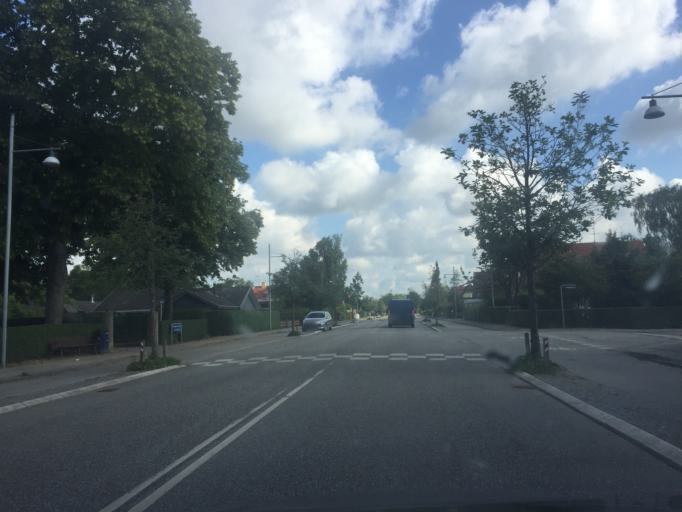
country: DK
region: Capital Region
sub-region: Glostrup Kommune
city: Glostrup
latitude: 55.6704
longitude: 12.4004
